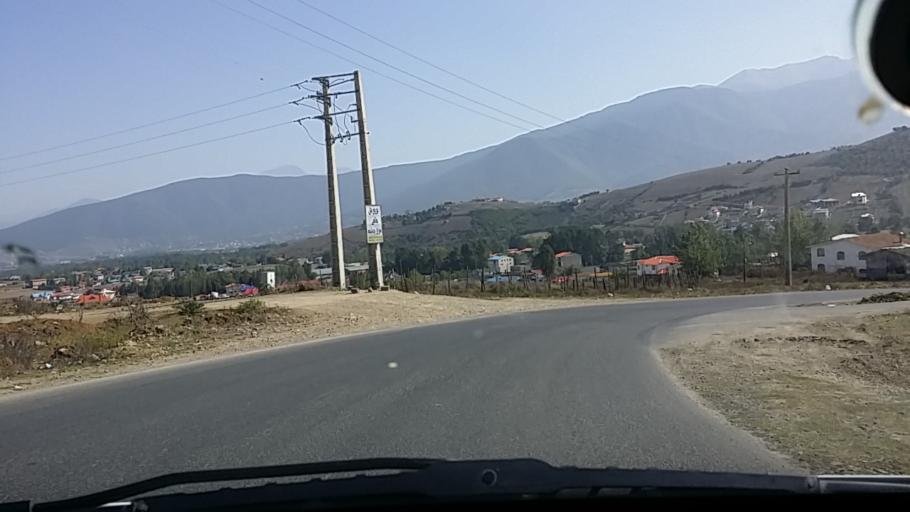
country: IR
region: Mazandaran
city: `Abbasabad
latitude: 36.5493
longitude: 51.1713
